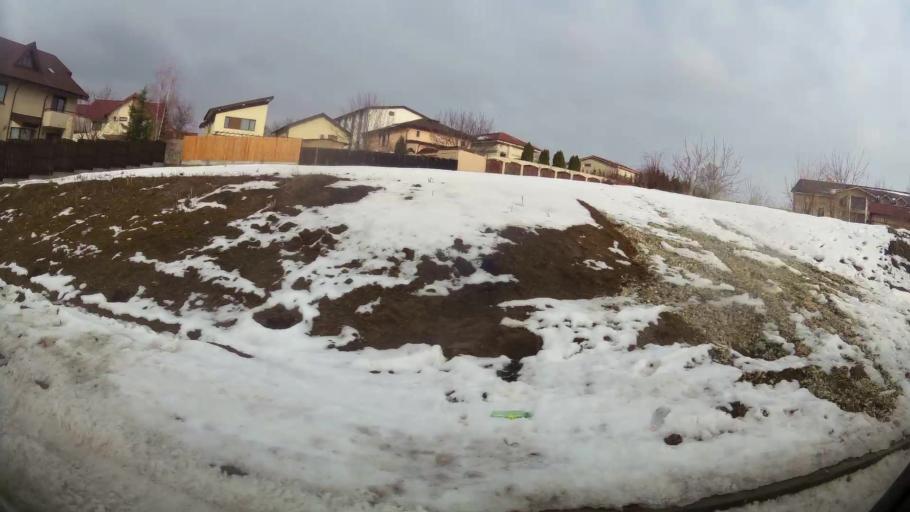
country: RO
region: Ilfov
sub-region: Comuna Popesti-Leordeni
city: Popesti-Leordeni
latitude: 44.4021
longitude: 26.1730
